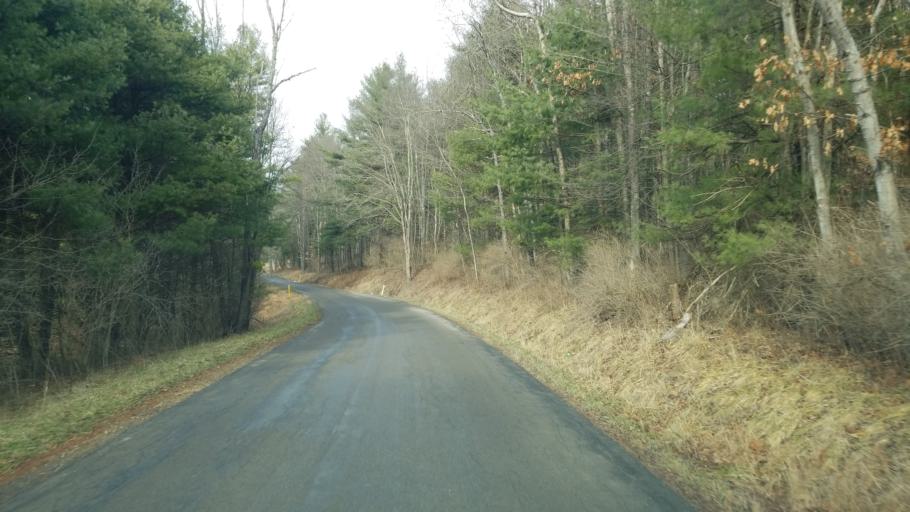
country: US
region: Pennsylvania
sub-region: Jefferson County
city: Punxsutawney
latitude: 40.8449
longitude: -78.9995
